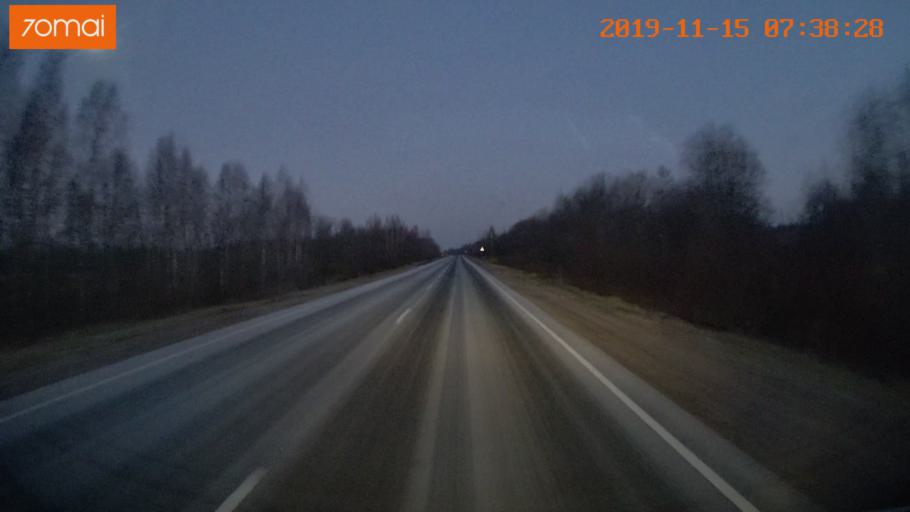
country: RU
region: Vologda
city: Sheksna
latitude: 58.7577
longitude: 38.4005
